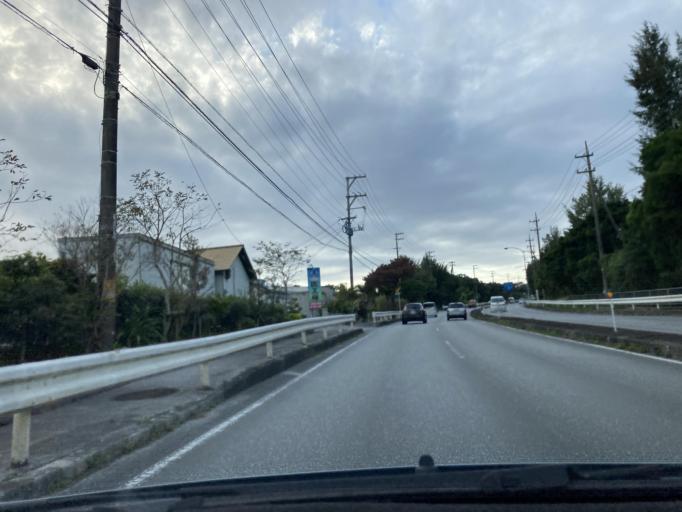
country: JP
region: Okinawa
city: Ishikawa
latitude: 26.4337
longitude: 127.8139
